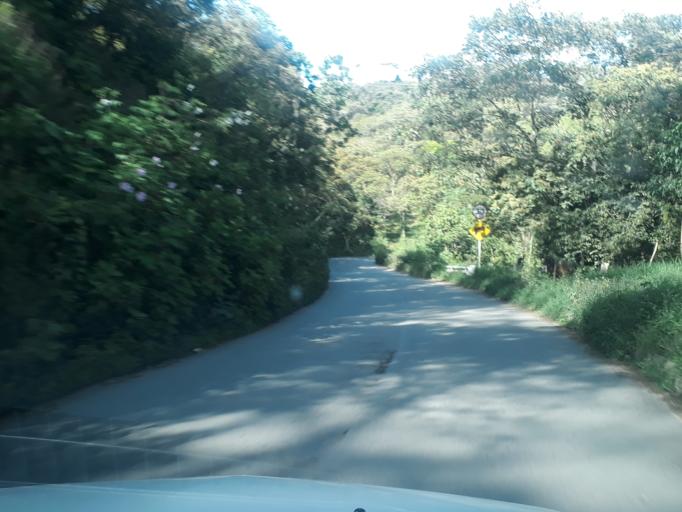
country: CO
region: Santander
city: Velez
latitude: 6.0218
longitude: -73.6621
